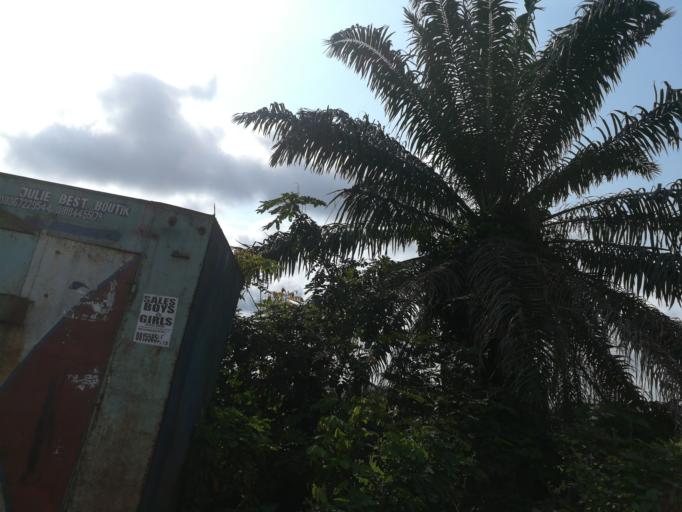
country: NG
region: Rivers
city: Okrika
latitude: 4.7458
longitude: 7.0807
